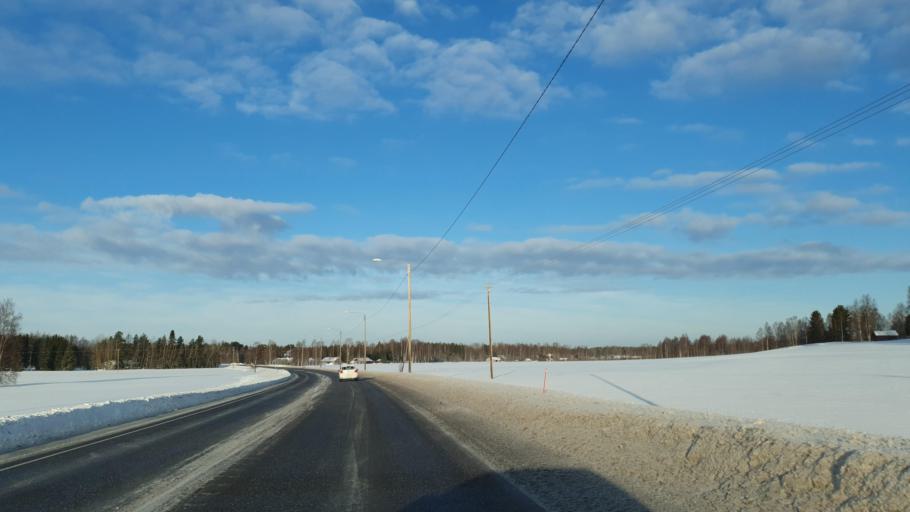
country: FI
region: Northern Ostrobothnia
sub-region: Oulu
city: Muhos
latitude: 64.7897
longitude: 26.1329
